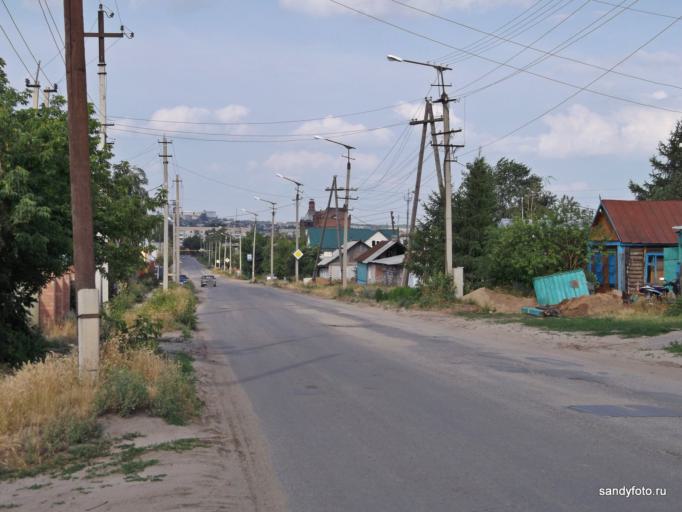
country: RU
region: Chelyabinsk
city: Troitsk
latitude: 54.0885
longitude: 61.5355
